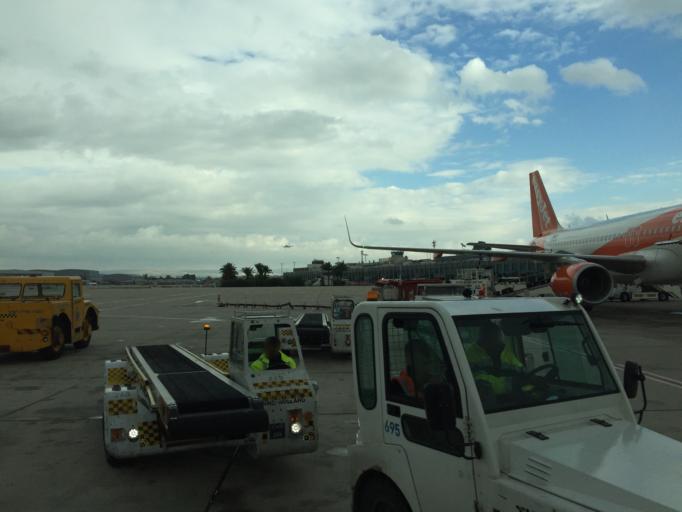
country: IL
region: Central District
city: Yehud
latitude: 31.9967
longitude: 34.8921
